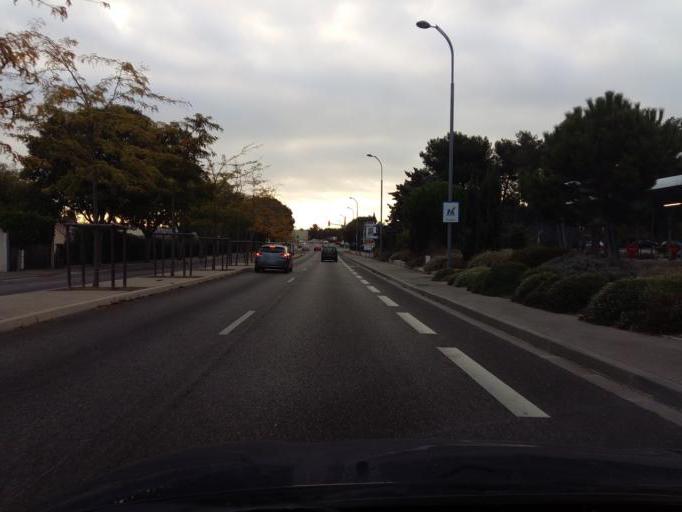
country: FR
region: Provence-Alpes-Cote d'Azur
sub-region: Departement des Bouches-du-Rhone
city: Martigues
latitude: 43.4239
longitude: 5.0547
